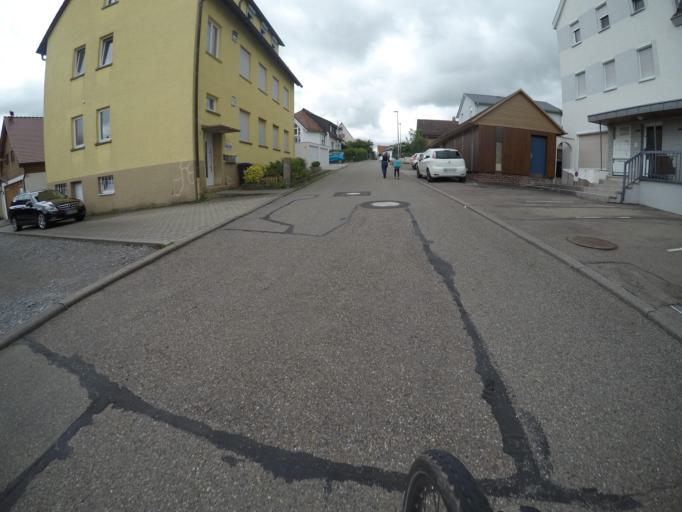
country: DE
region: Baden-Wuerttemberg
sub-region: Regierungsbezirk Stuttgart
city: Unterjettingen
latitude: 48.5646
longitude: 8.7821
